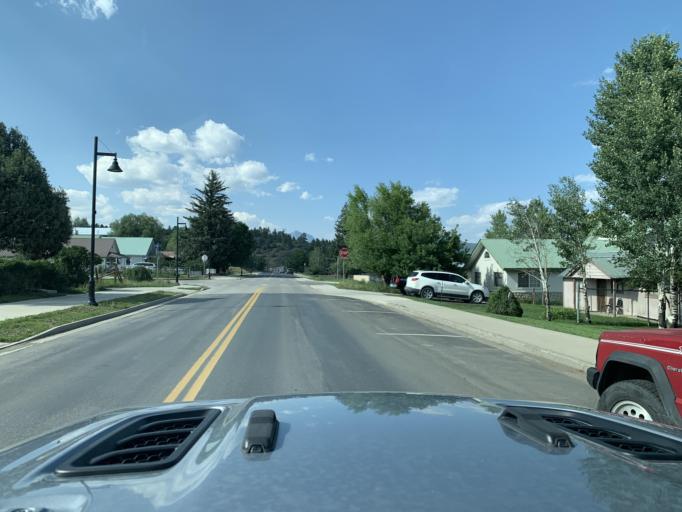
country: US
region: Colorado
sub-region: Archuleta County
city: Pagosa Springs
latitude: 37.2625
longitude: -107.0172
